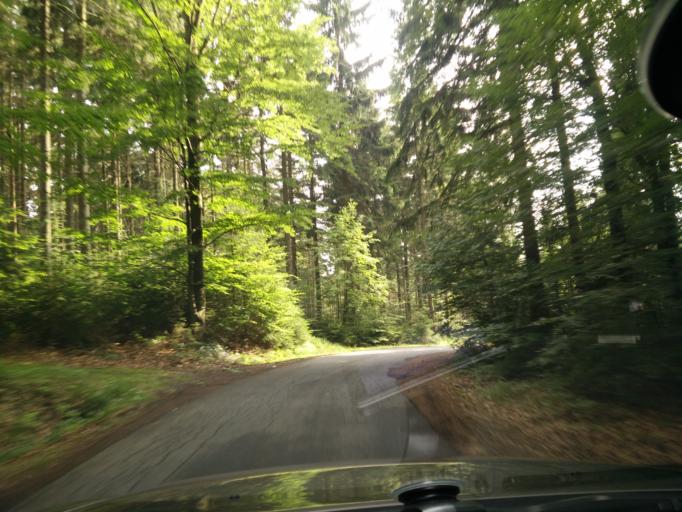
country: DE
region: Bavaria
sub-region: Upper Franconia
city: Fichtelberg
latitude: 50.0132
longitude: 11.8627
